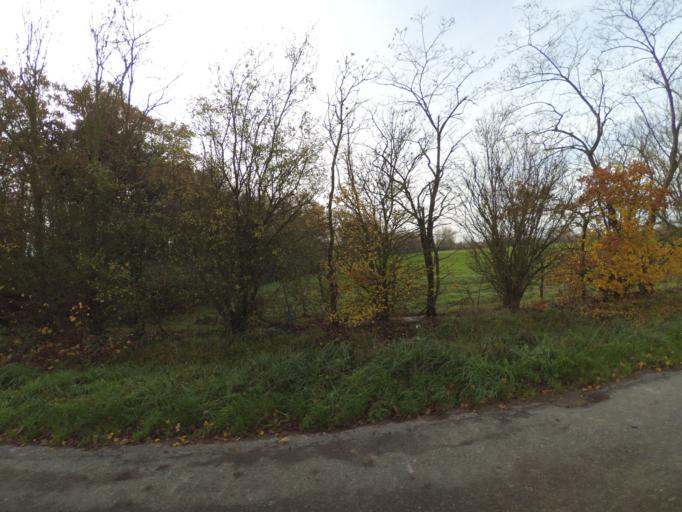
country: FR
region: Pays de la Loire
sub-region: Departement de la Loire-Atlantique
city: La Planche
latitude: 47.0102
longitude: -1.4075
